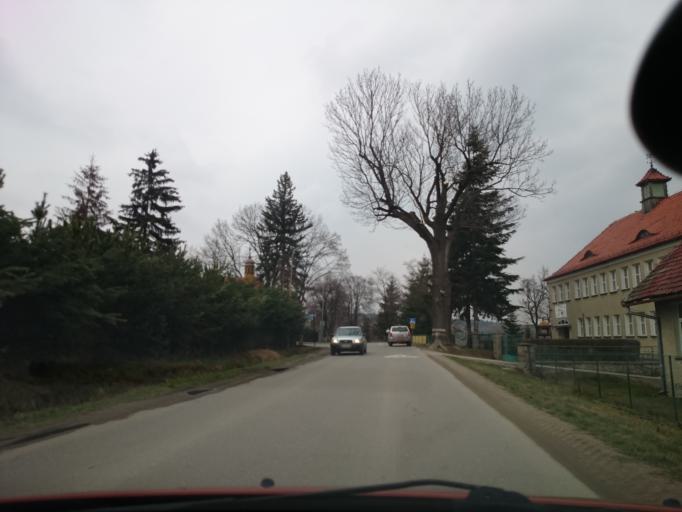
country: PL
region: Lower Silesian Voivodeship
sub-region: Powiat klodzki
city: Polanica-Zdroj
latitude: 50.3934
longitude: 16.5220
